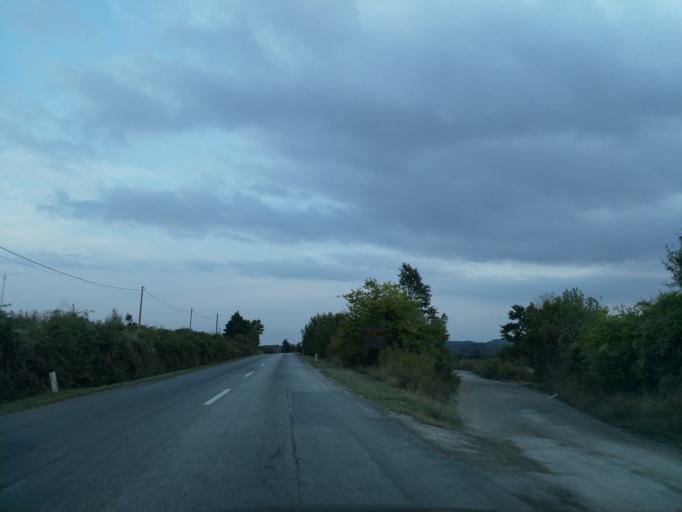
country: RS
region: Central Serbia
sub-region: Sumadijski Okrug
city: Topola
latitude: 44.1415
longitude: 20.7439
